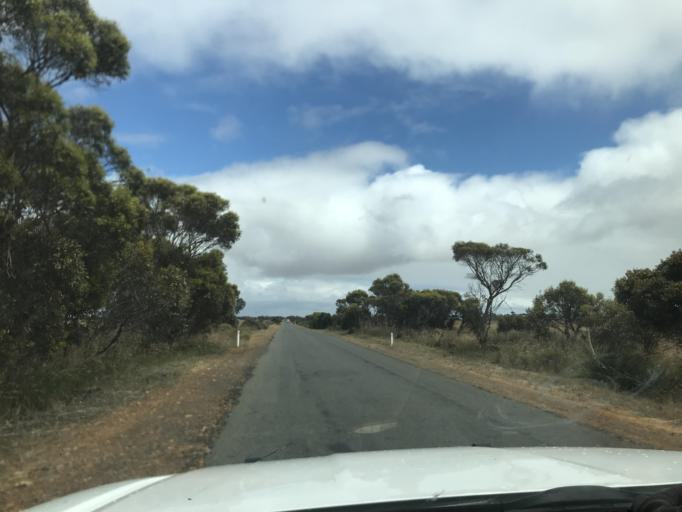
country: AU
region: South Australia
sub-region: Tatiara
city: Bordertown
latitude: -36.1387
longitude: 141.2121
